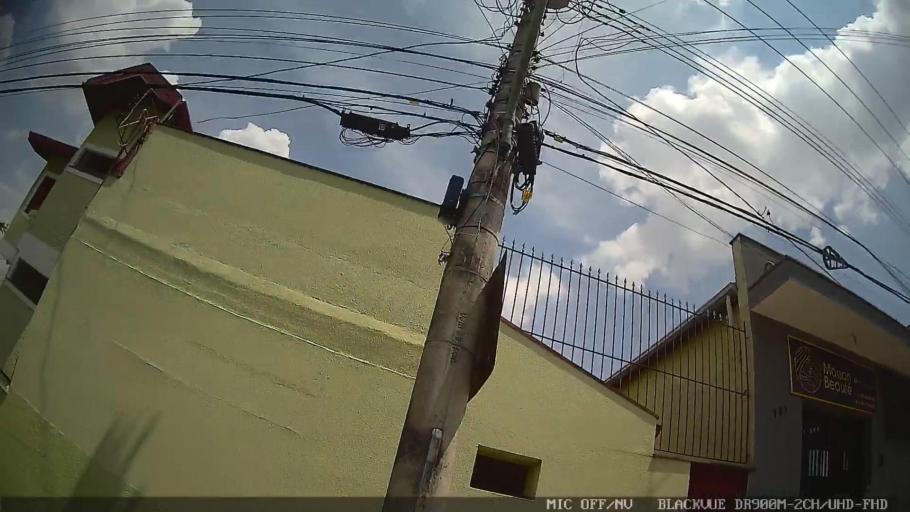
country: BR
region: Sao Paulo
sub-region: Itatiba
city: Itatiba
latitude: -23.0118
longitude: -46.8453
